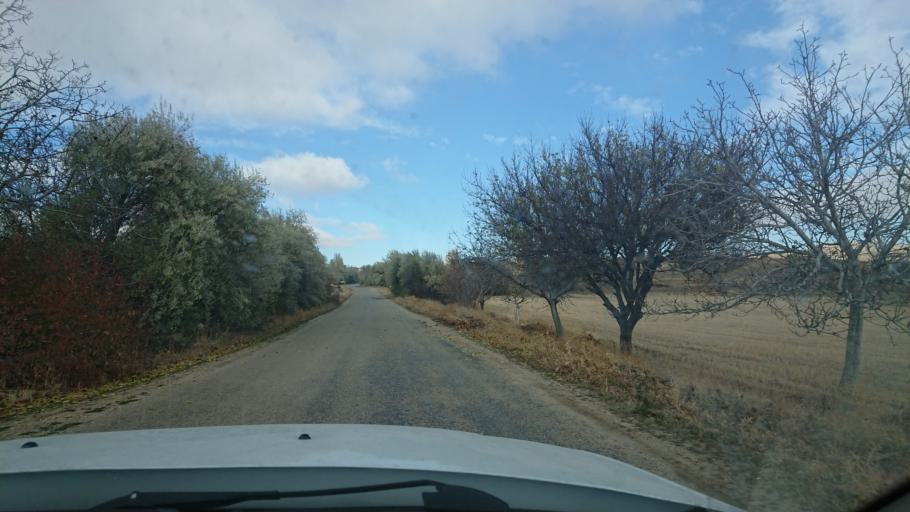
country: TR
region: Aksaray
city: Agacoren
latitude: 38.8281
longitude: 33.9574
